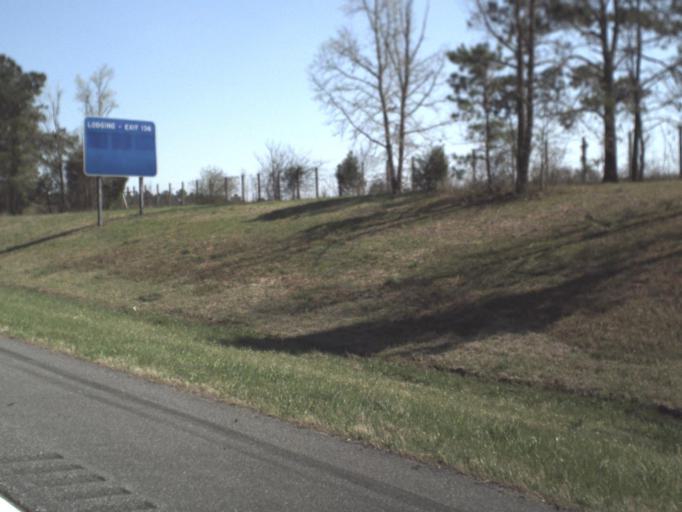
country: US
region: Florida
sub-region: Jackson County
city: Marianna
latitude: 30.7573
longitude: -85.2850
